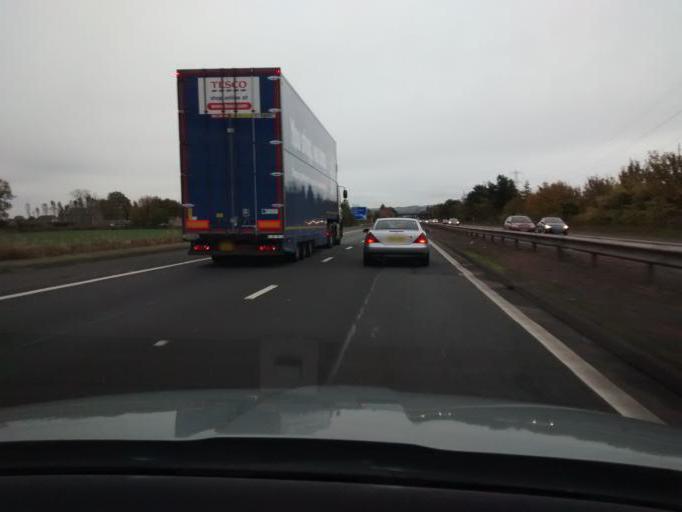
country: GB
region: Scotland
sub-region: Falkirk
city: Airth
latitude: 56.0338
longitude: -3.7668
